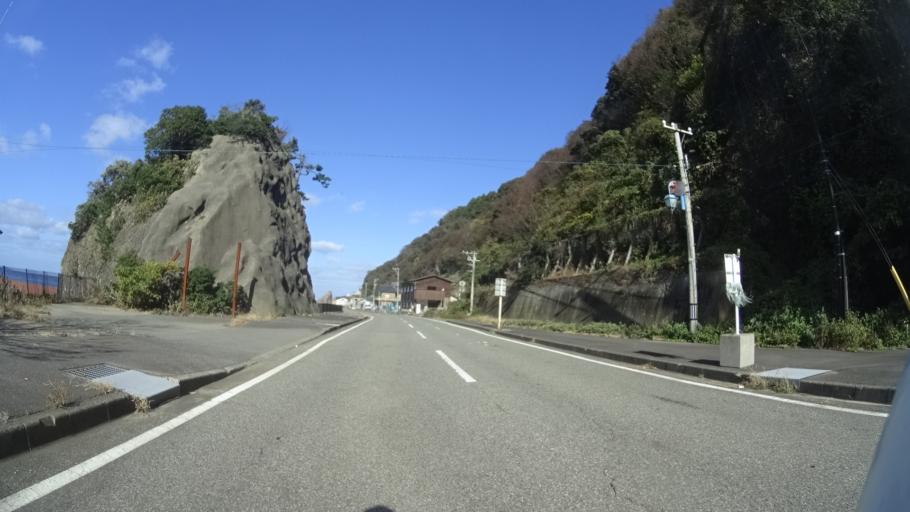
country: JP
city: Asahi
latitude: 35.8798
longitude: 136.0030
